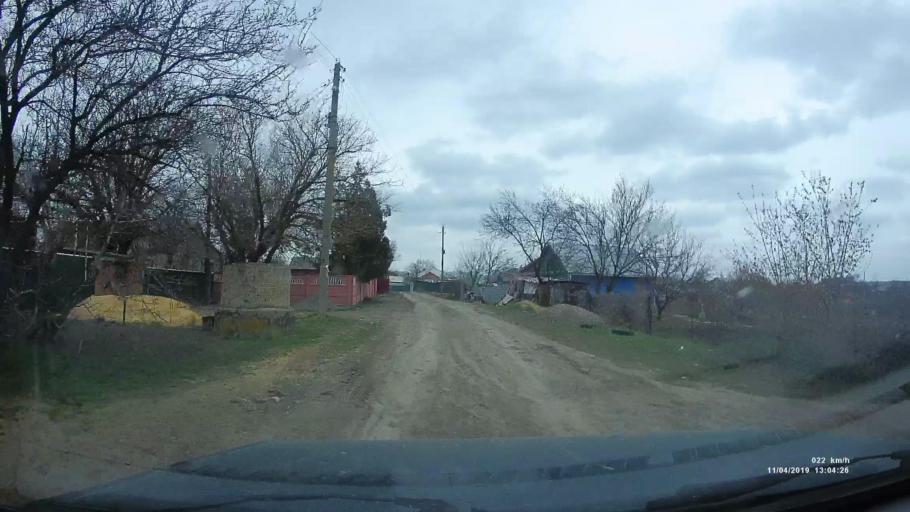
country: RU
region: Rostov
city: Staraya Stanitsa
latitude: 48.2871
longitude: 40.3469
